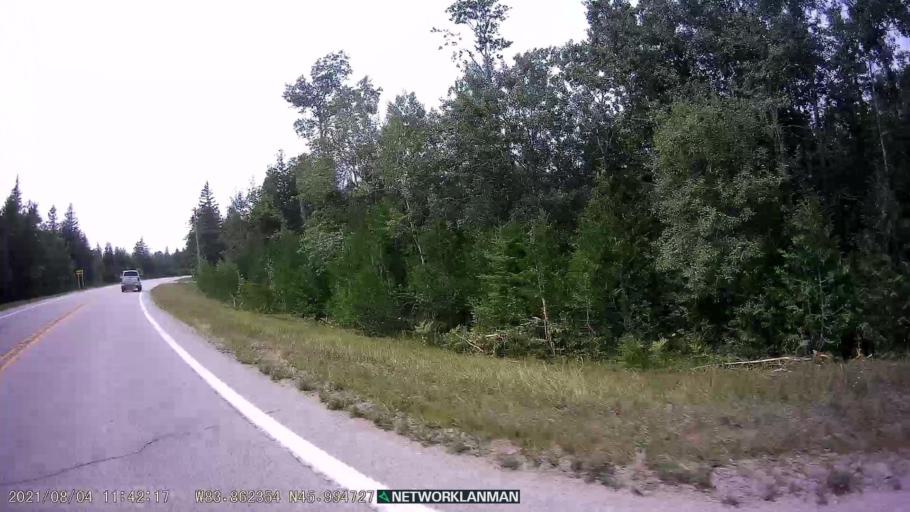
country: CA
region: Ontario
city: Thessalon
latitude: 45.9945
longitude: -83.8630
